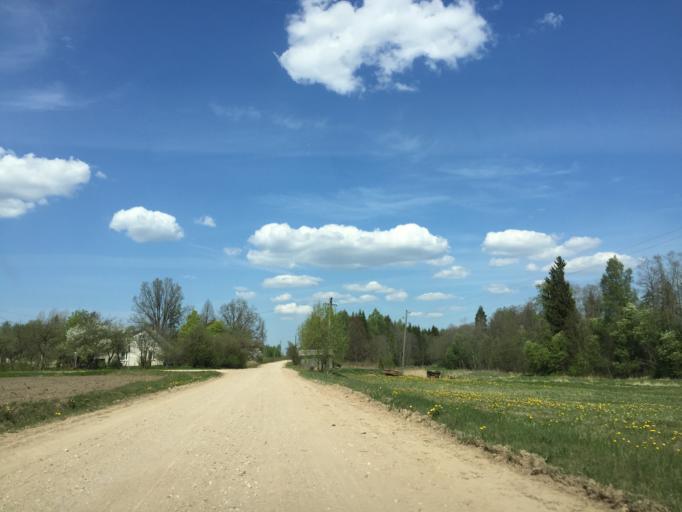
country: LV
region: Limbazu Rajons
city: Limbazi
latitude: 57.3639
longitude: 24.6376
